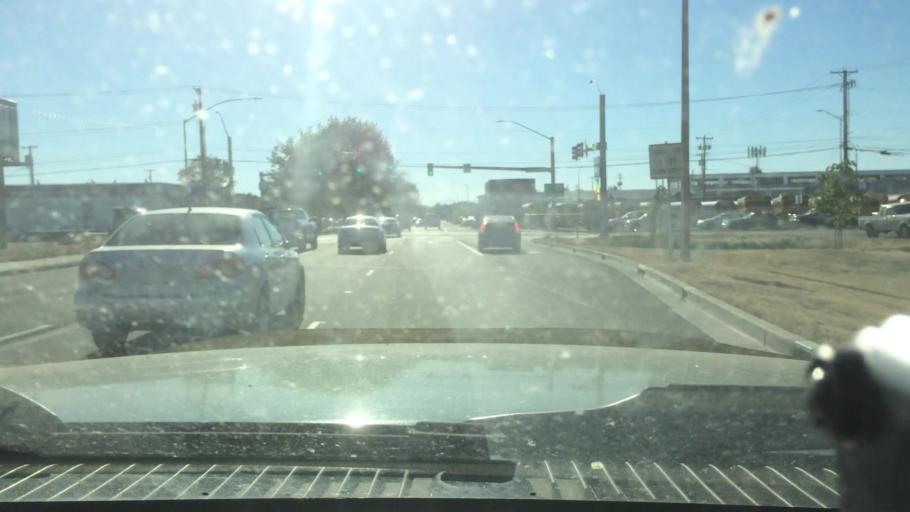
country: US
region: Oregon
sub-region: Lane County
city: Eugene
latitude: 44.0521
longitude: -123.1237
